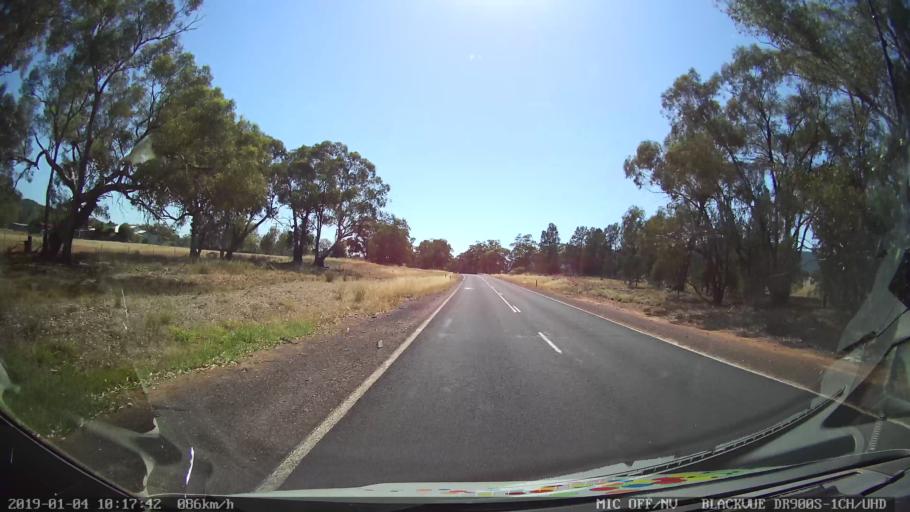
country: AU
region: New South Wales
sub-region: Cabonne
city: Canowindra
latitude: -33.3838
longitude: 148.4555
